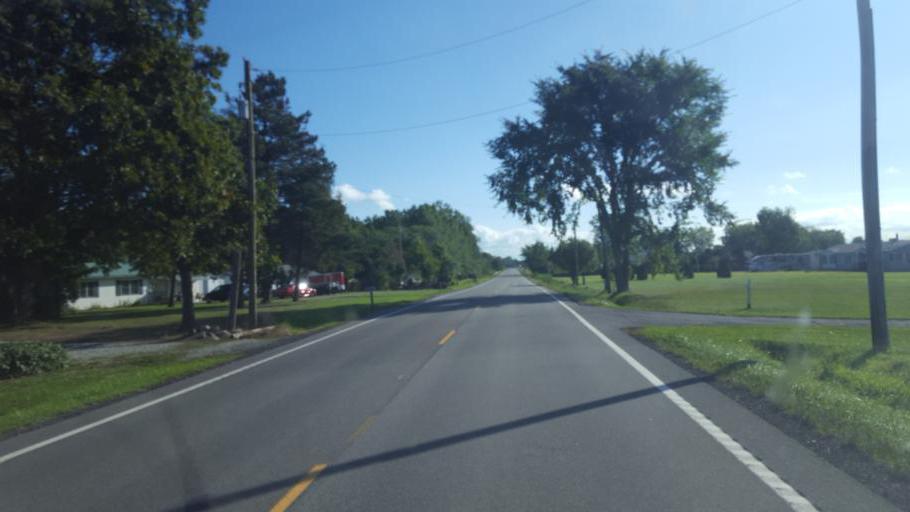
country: US
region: Ohio
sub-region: Lorain County
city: Oberlin
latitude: 41.2912
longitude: -82.2679
